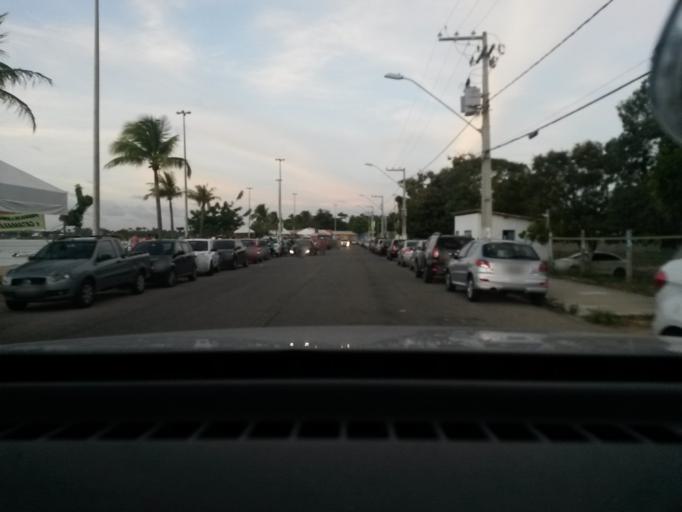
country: BR
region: Sergipe
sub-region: Sao Cristovao
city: Sao Cristovao
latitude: -11.1011
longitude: -37.1502
